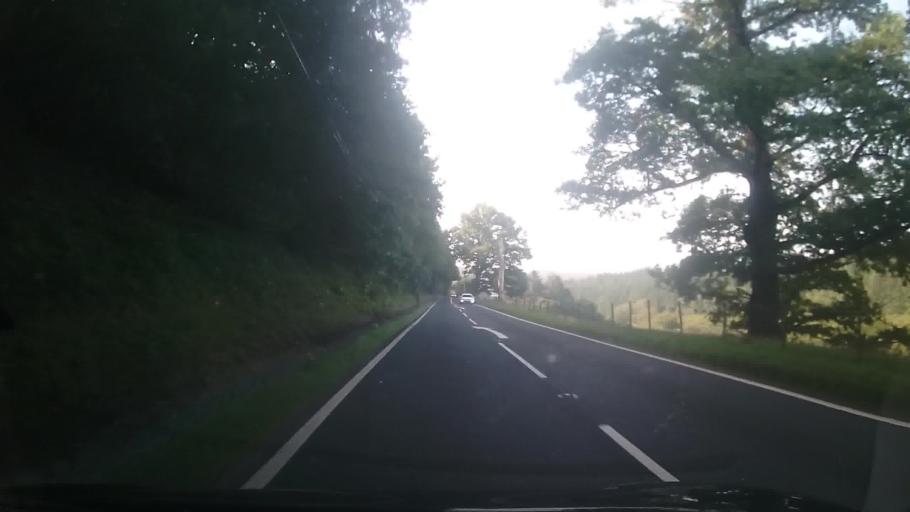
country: GB
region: Wales
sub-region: Sir Powys
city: Rhayader
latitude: 52.2899
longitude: -3.5016
